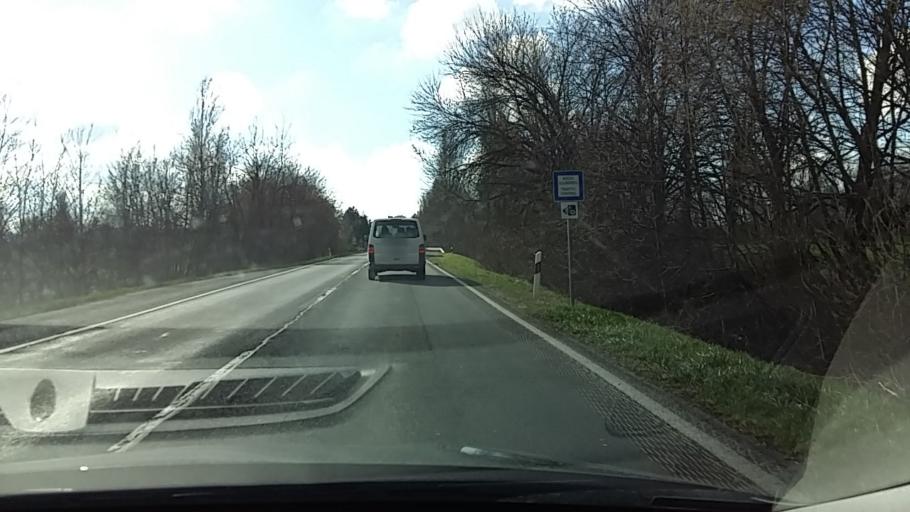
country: HU
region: Veszprem
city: Tapolca
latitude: 46.8376
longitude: 17.3725
